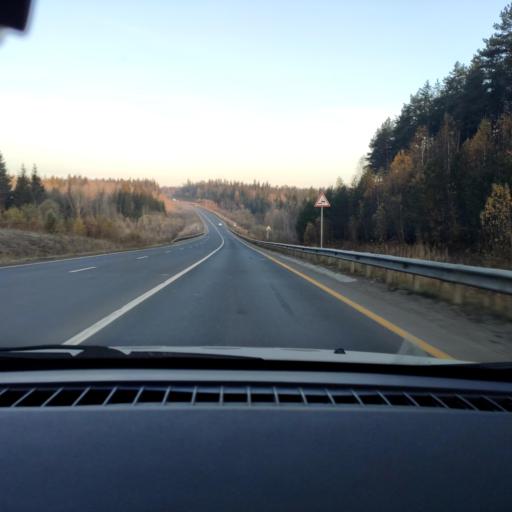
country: RU
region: Perm
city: Novyye Lyady
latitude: 58.0365
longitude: 56.4716
